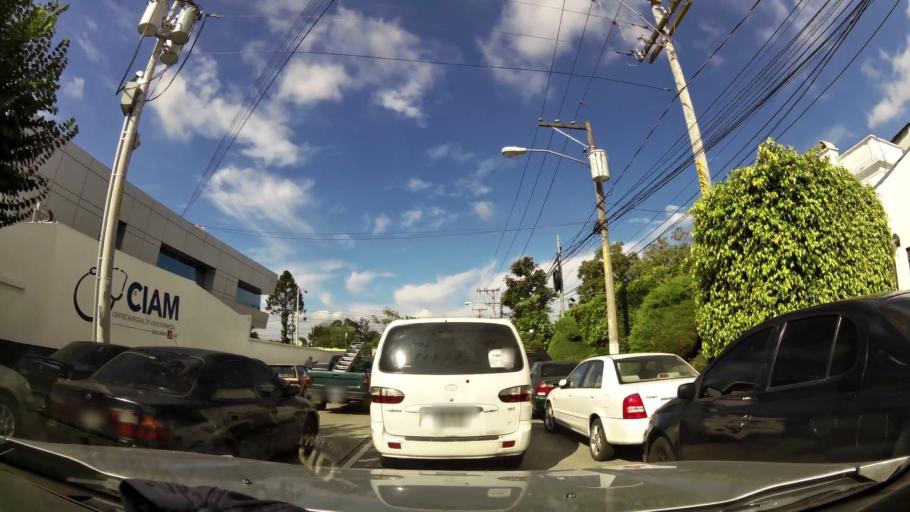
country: GT
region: Guatemala
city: Guatemala City
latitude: 14.6025
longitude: -90.5181
